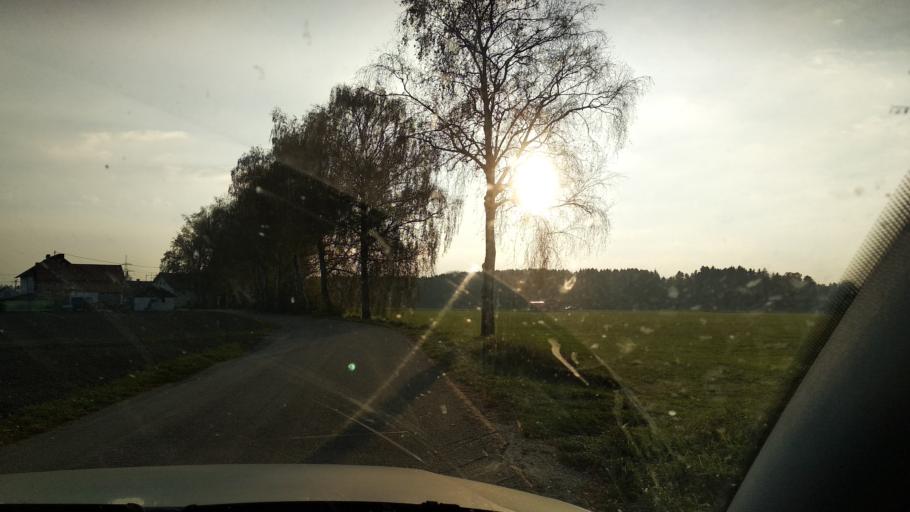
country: DE
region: Bavaria
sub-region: Upper Bavaria
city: Ottenhofen
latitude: 48.2176
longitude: 11.8943
